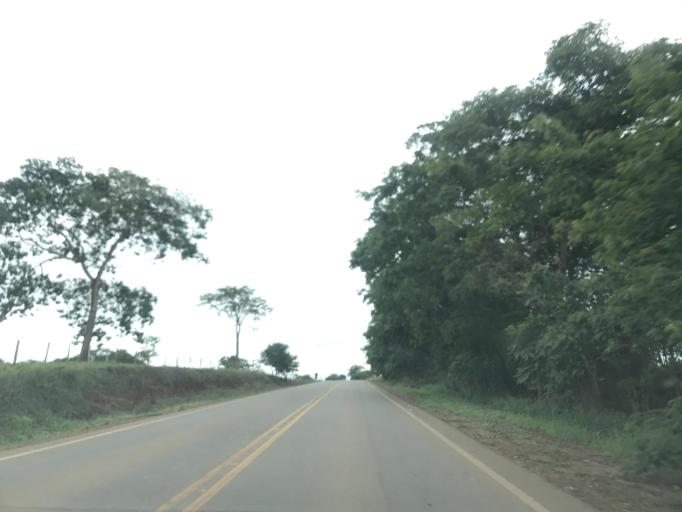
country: BR
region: Goias
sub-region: Vianopolis
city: Vianopolis
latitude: -16.7102
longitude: -48.3991
